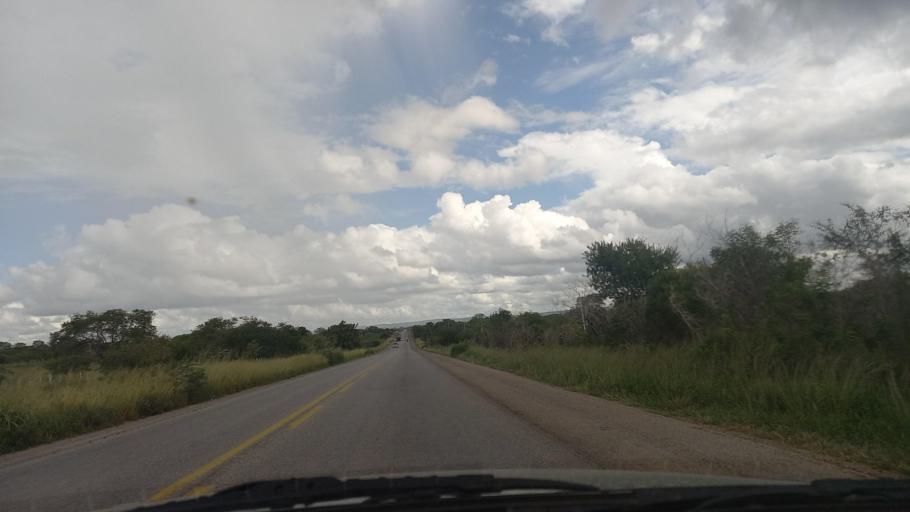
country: BR
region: Pernambuco
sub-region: Cachoeirinha
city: Cachoeirinha
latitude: -8.5398
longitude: -36.2683
